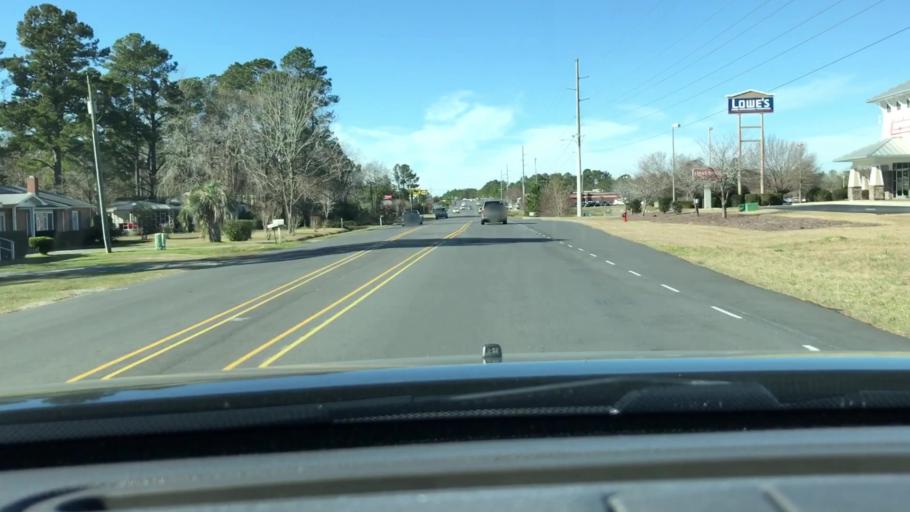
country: US
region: North Carolina
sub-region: Brunswick County
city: Shallotte
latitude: 33.9725
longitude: -78.3986
